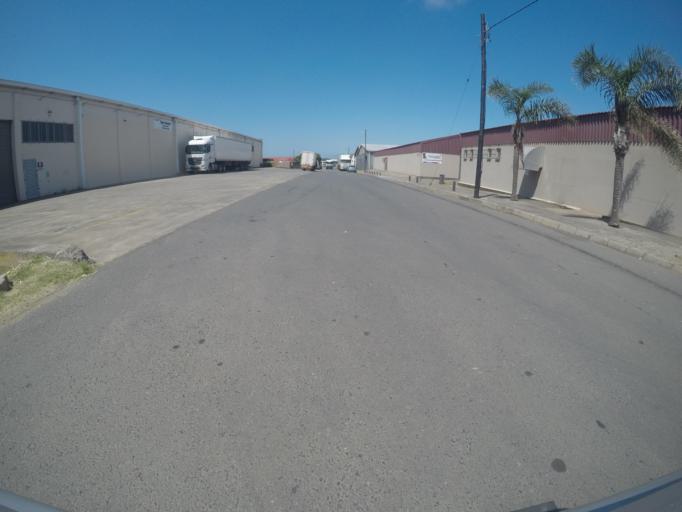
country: ZA
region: Eastern Cape
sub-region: Buffalo City Metropolitan Municipality
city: East London
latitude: -33.0085
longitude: 27.9107
